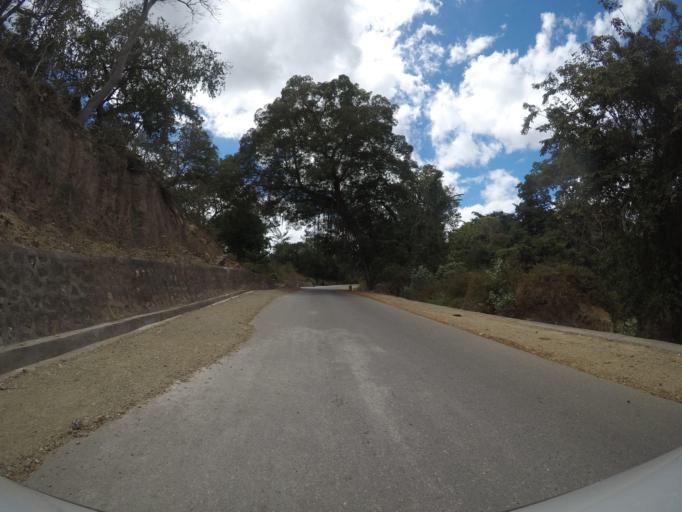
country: TL
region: Lautem
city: Lospalos
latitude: -8.3540
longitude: 126.9279
